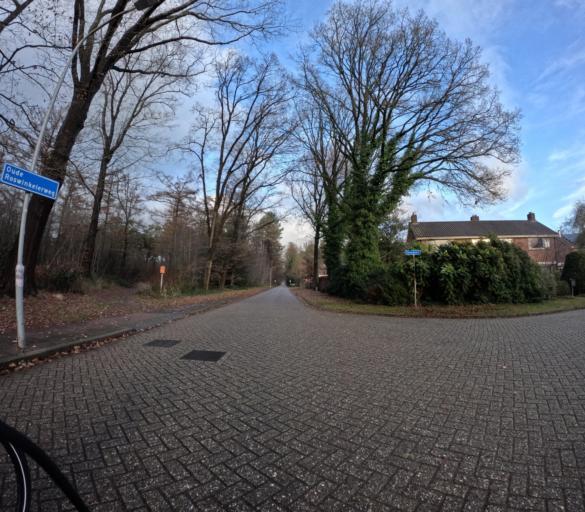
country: NL
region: Drenthe
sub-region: Gemeente Emmen
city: Emmen
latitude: 52.7994
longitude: 6.9086
